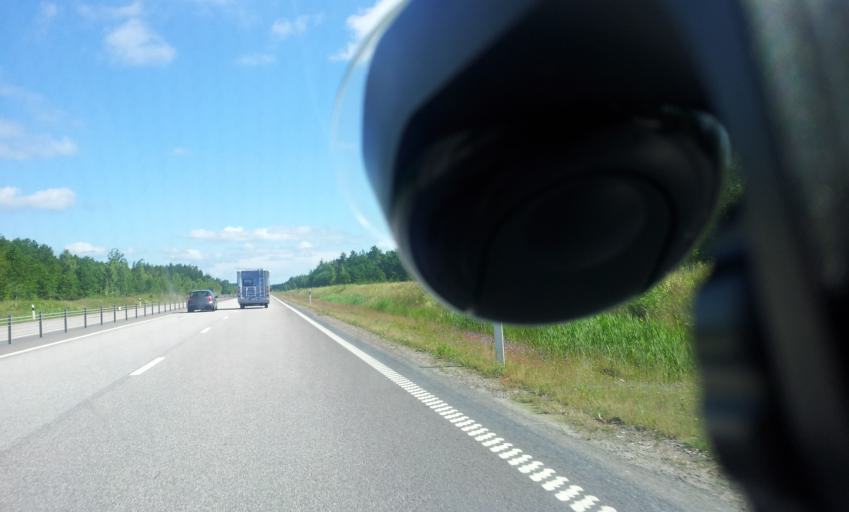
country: SE
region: Kalmar
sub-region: Monsteras Kommun
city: Timmernabben
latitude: 56.9689
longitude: 16.3951
